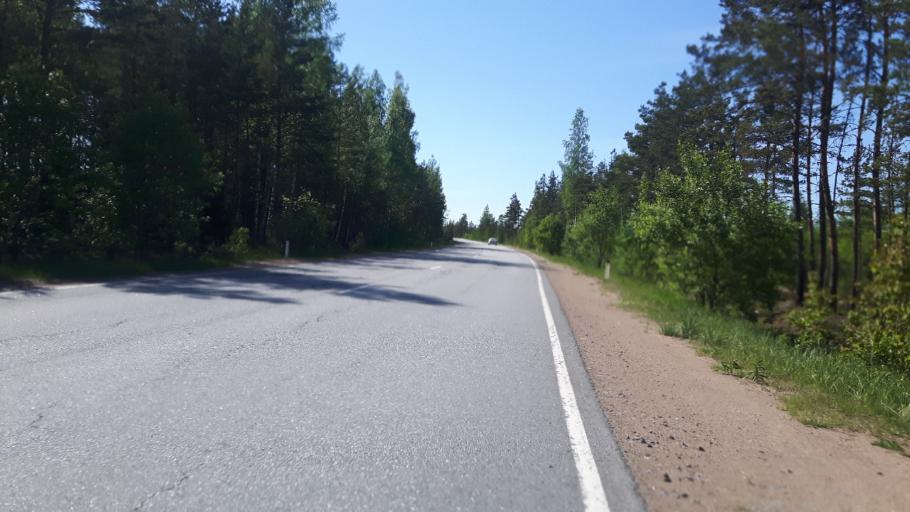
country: RU
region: Leningrad
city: Sista-Palkino
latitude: 59.7691
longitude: 28.7918
